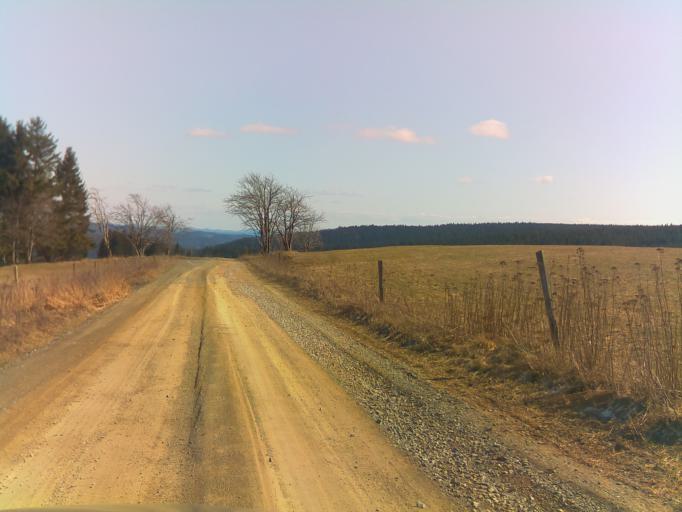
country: DE
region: Thuringia
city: Steinheid
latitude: 50.4585
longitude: 11.0963
